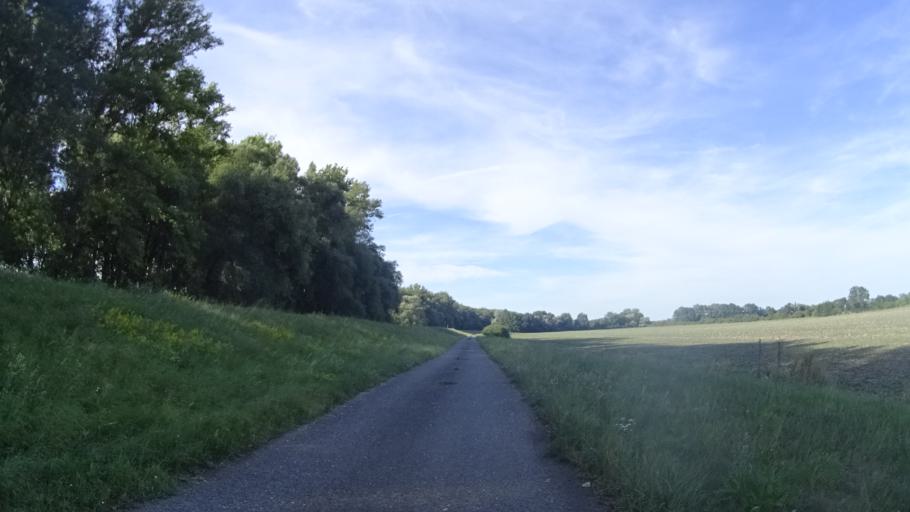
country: AT
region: Lower Austria
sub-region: Politischer Bezirk Ganserndorf
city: Drosing
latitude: 48.5329
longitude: 16.9566
